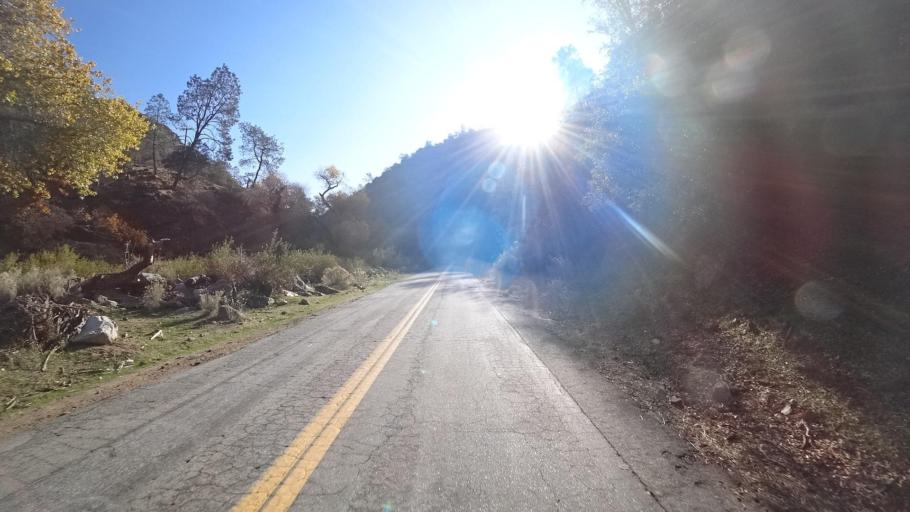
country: US
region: California
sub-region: Kern County
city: Golden Hills
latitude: 35.3079
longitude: -118.4968
